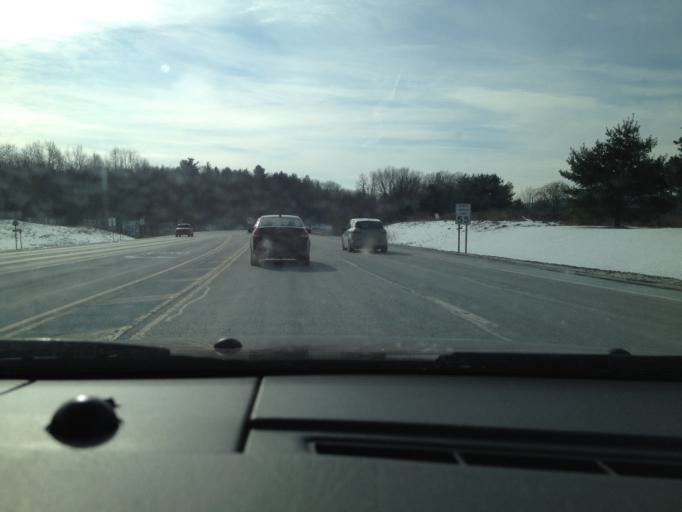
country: US
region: New York
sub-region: Rensselaer County
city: Hampton Manor
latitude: 42.6542
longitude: -73.6994
